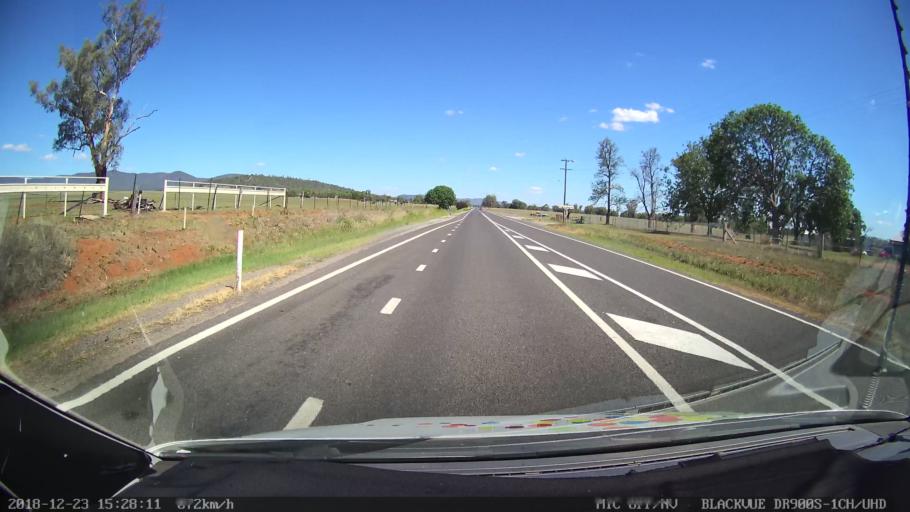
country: AU
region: New South Wales
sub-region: Tamworth Municipality
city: East Tamworth
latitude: -30.9339
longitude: 150.8504
